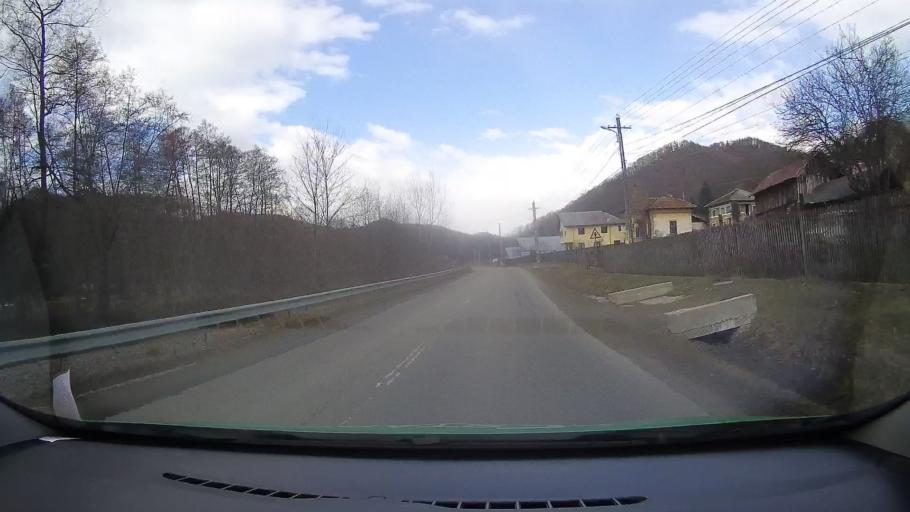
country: RO
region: Dambovita
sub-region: Comuna Varfuri
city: Varfuri
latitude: 45.0768
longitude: 25.5215
